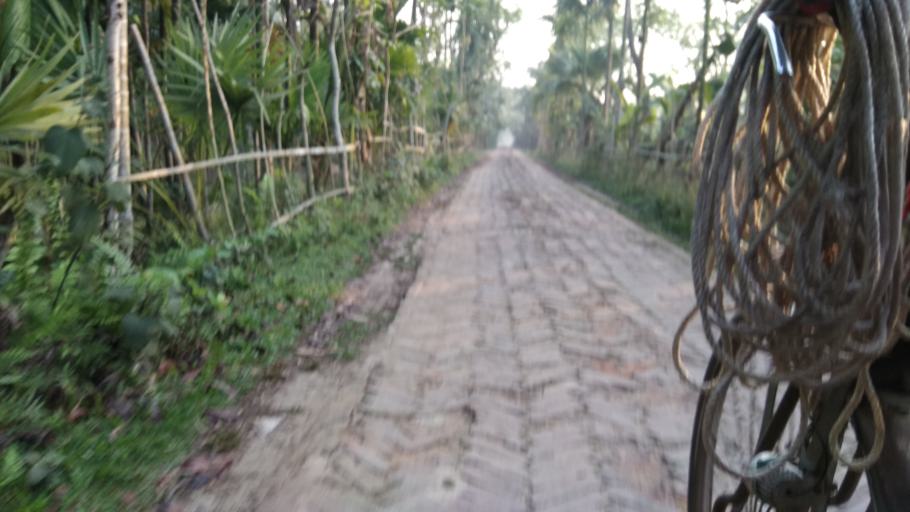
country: BD
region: Barisal
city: Mehendiganj
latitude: 22.9276
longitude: 90.4068
